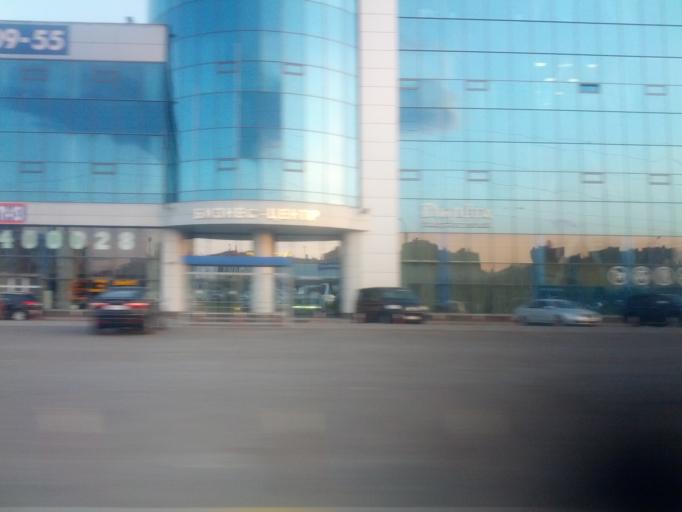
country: RU
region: St.-Petersburg
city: Staraya Derevnya
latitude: 59.9961
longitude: 30.2488
